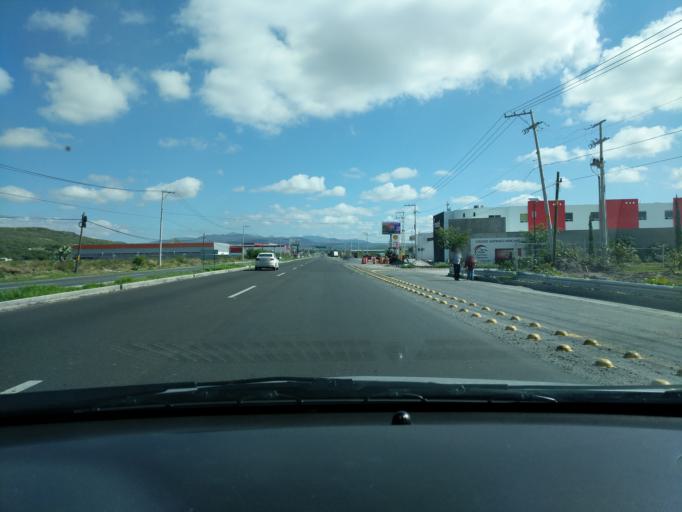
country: MX
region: Queretaro
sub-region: Queretaro
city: Patria Nueva
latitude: 20.6357
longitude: -100.4997
